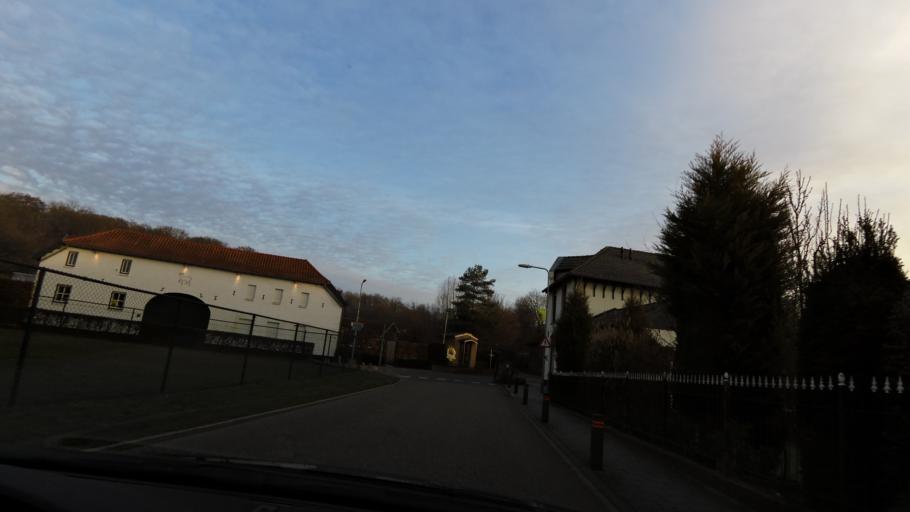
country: NL
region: Limburg
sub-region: Gemeente Schinnen
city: Puth
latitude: 50.9434
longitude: 5.8755
